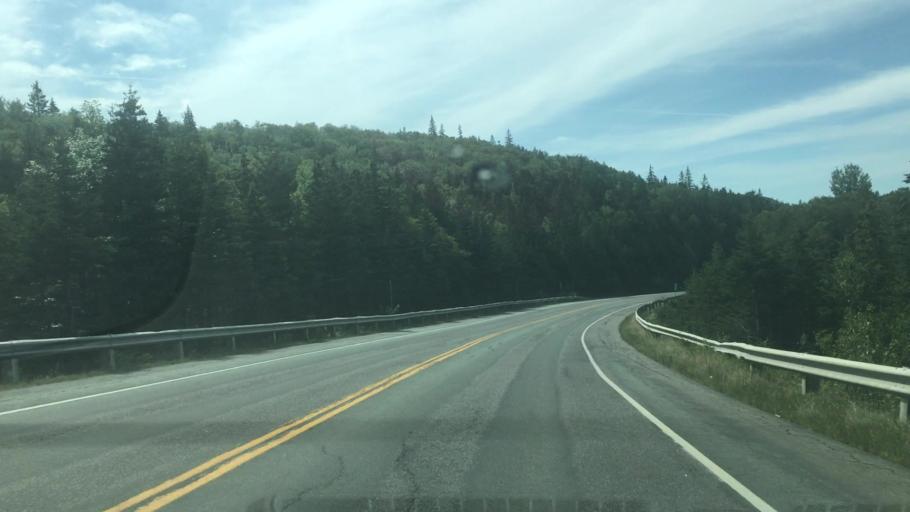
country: CA
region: Nova Scotia
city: Sydney Mines
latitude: 46.2408
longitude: -60.5607
